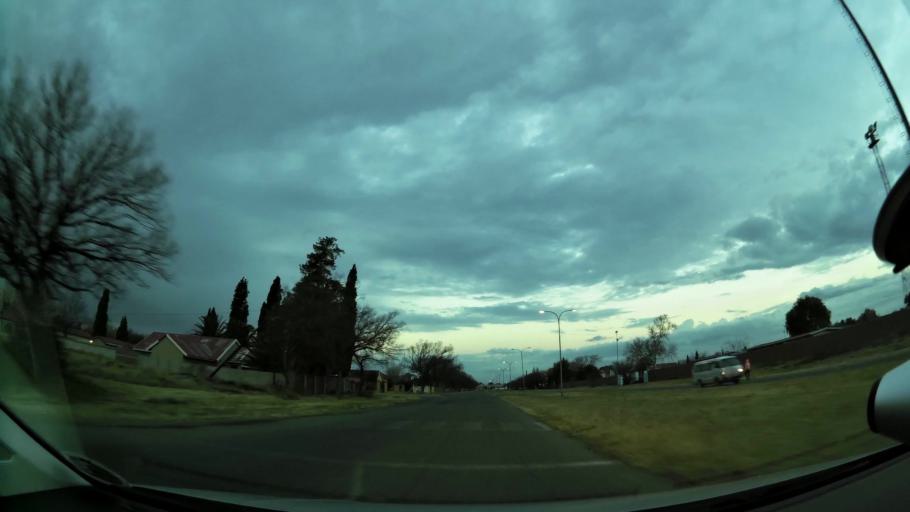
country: ZA
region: Orange Free State
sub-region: Lejweleputswa District Municipality
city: Welkom
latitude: -27.9772
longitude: 26.7536
